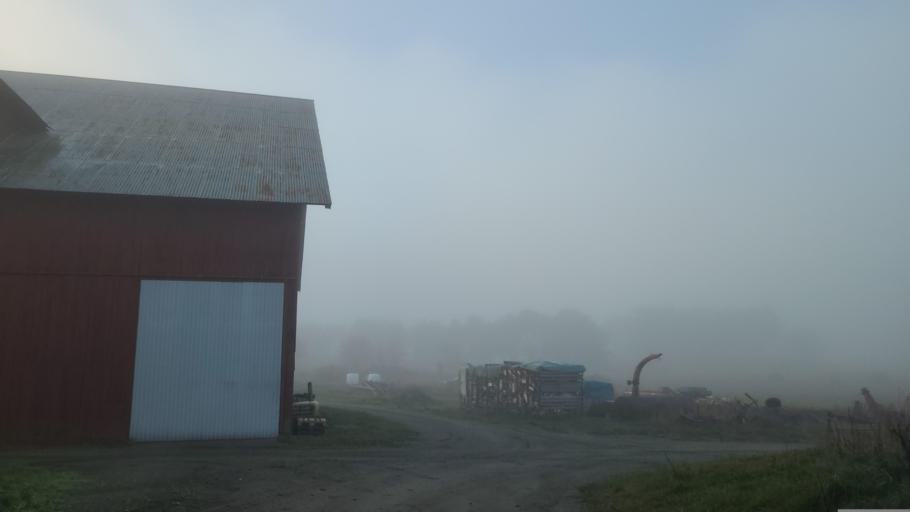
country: SE
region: Uppsala
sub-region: Enkopings Kommun
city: Grillby
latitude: 59.5976
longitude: 17.1757
